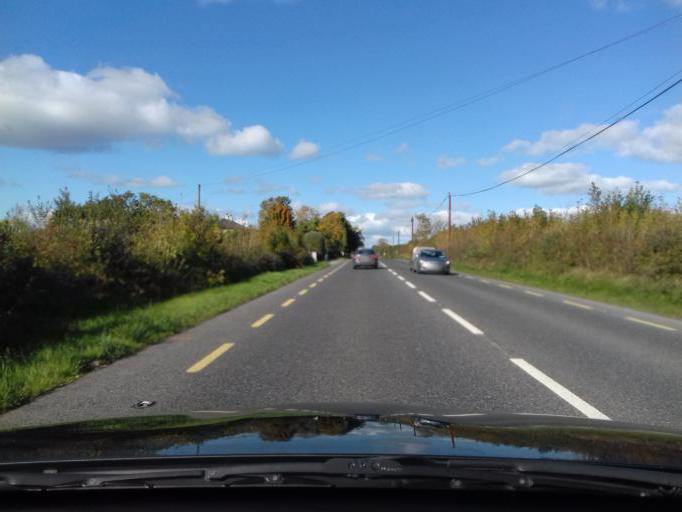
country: IE
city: Kentstown
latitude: 53.6448
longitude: -6.5058
